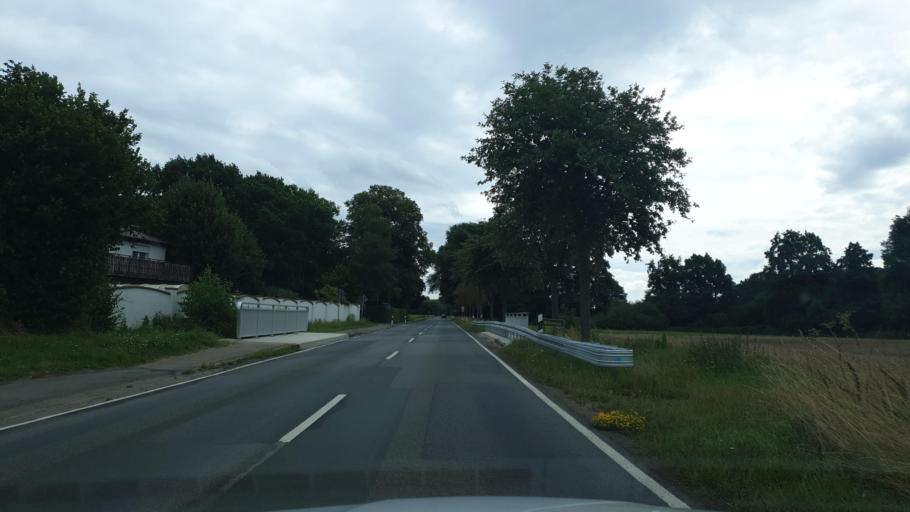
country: DE
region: Lower Saxony
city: Hagen
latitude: 52.2302
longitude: 7.9949
